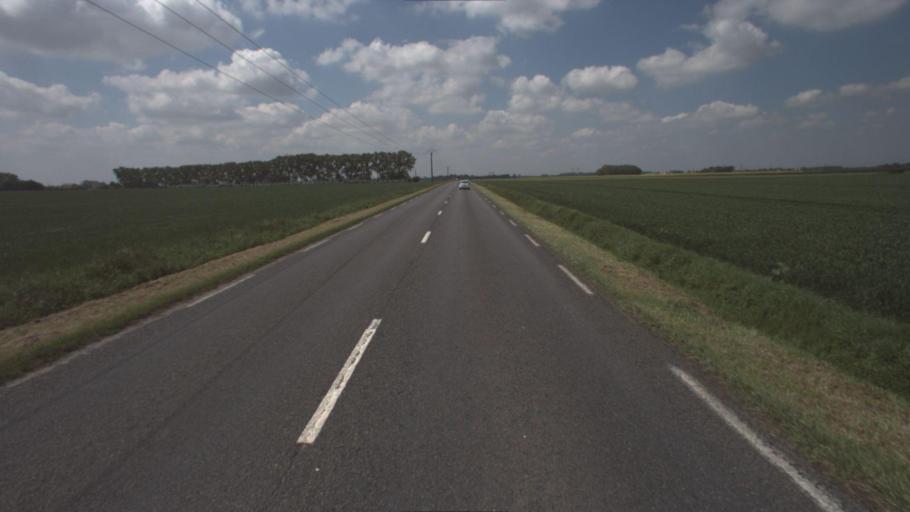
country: FR
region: Ile-de-France
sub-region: Departement de Seine-et-Marne
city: Guignes
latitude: 48.6246
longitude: 2.7672
